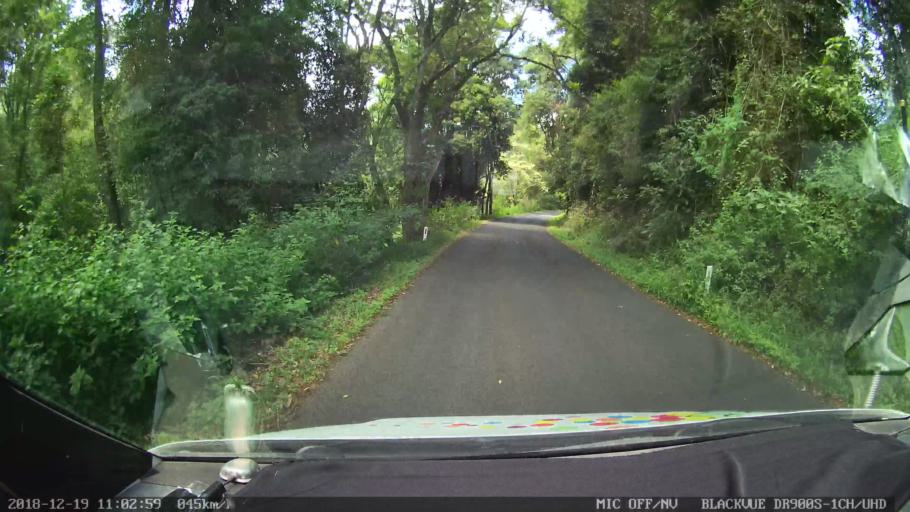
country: AU
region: New South Wales
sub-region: Lismore Municipality
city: Nimbin
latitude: -28.6091
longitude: 153.2700
